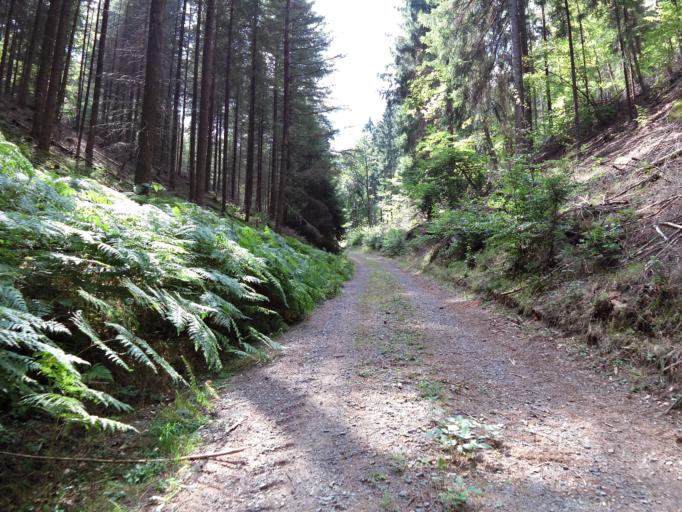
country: DE
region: Rheinland-Pfalz
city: Frankenstein
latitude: 49.4655
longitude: 8.0029
